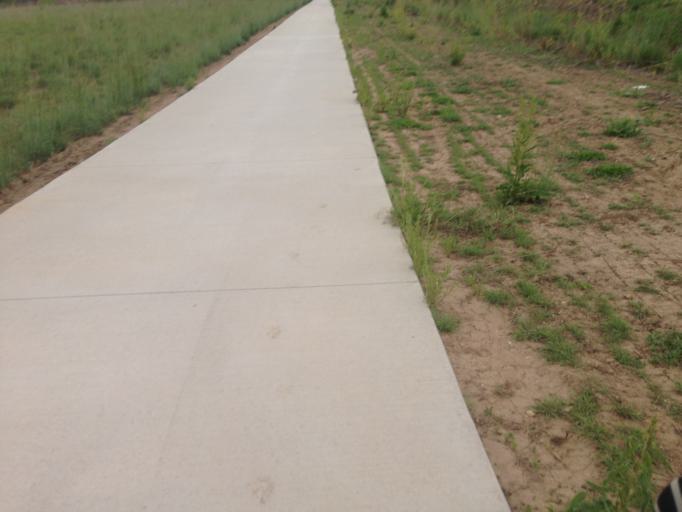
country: US
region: Colorado
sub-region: Boulder County
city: Longmont
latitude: 40.1481
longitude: -105.0966
